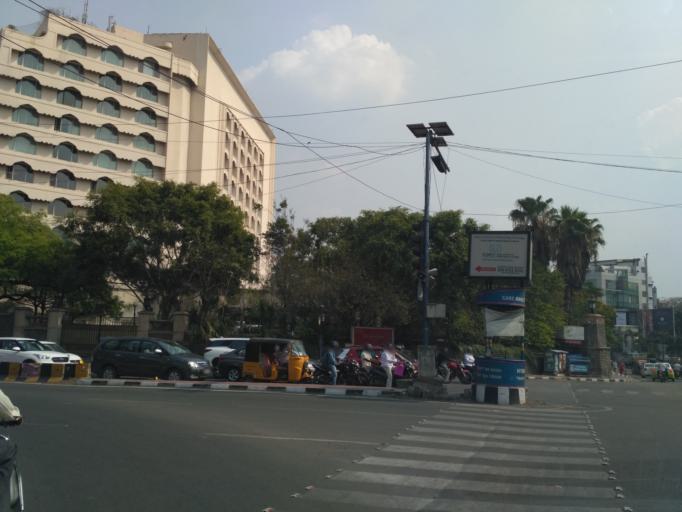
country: IN
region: Telangana
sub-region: Hyderabad
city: Hyderabad
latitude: 17.4172
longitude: 78.4491
